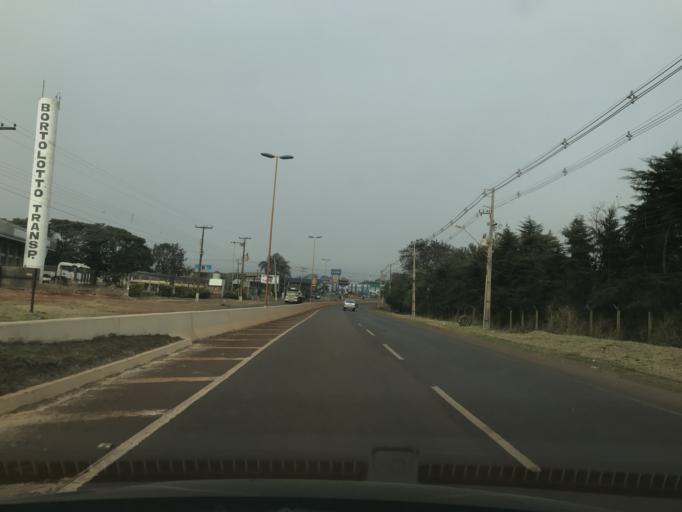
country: BR
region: Parana
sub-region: Toledo
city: Toledo
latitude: -24.7135
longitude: -53.7036
